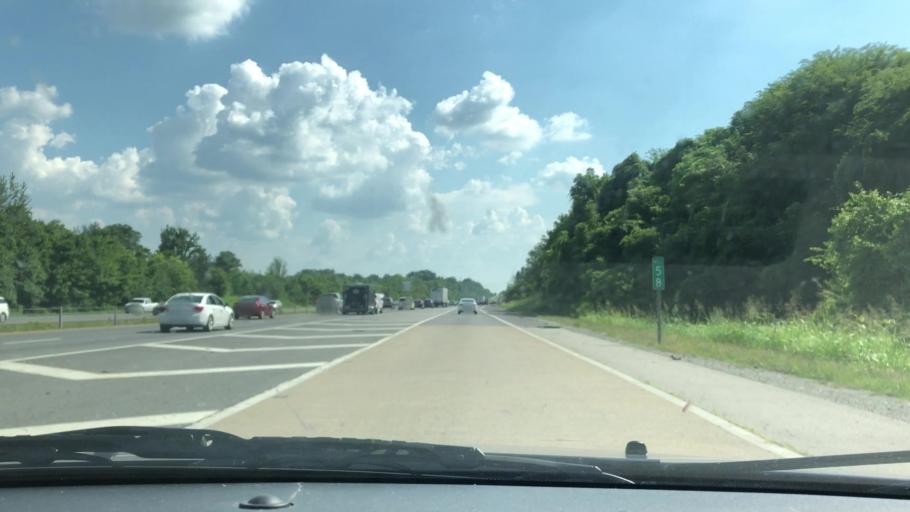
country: US
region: Tennessee
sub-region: Williamson County
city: Thompson's Station
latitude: 35.8100
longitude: -86.8474
